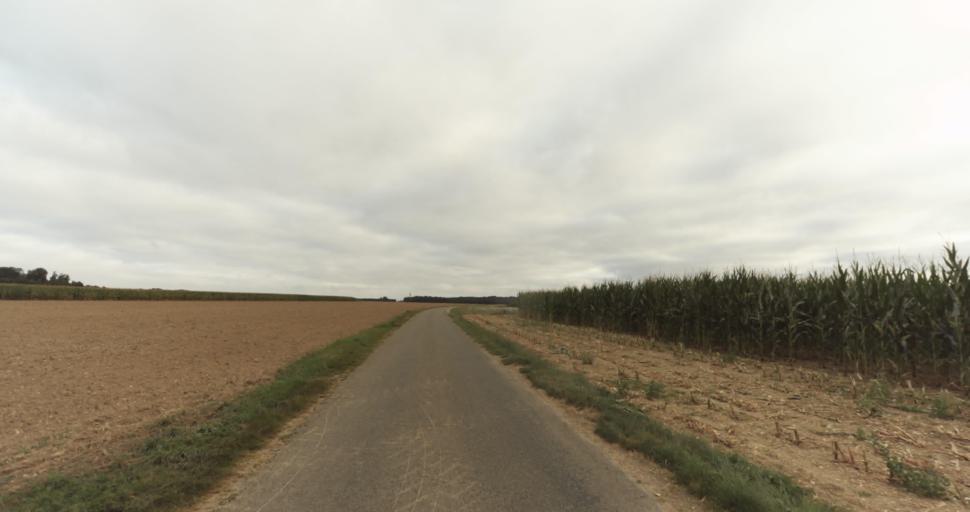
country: FR
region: Haute-Normandie
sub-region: Departement de l'Eure
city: Saint-Germain-sur-Avre
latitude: 48.7844
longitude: 1.2607
